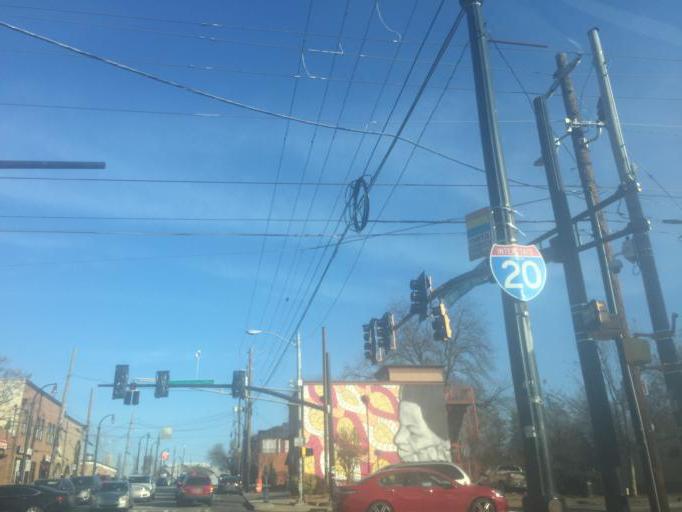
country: US
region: Georgia
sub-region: Fulton County
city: Atlanta
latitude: 33.7547
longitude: -84.4178
